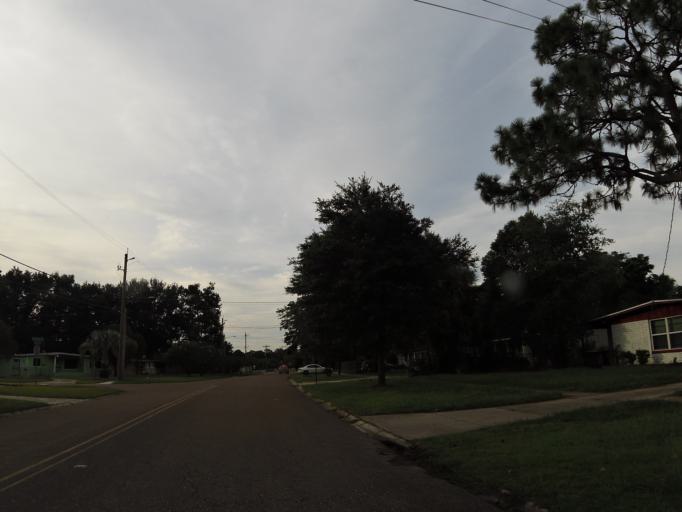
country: US
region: Florida
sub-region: Duval County
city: Jacksonville
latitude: 30.4004
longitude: -81.7197
